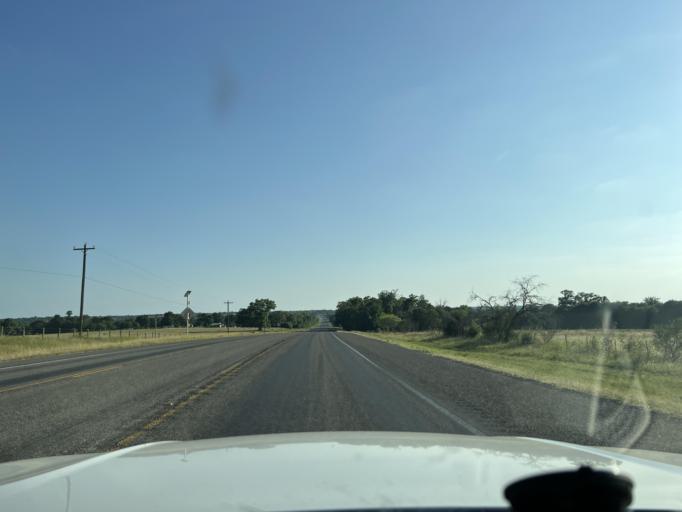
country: US
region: Texas
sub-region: Washington County
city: Brenham
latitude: 30.2337
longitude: -96.2876
